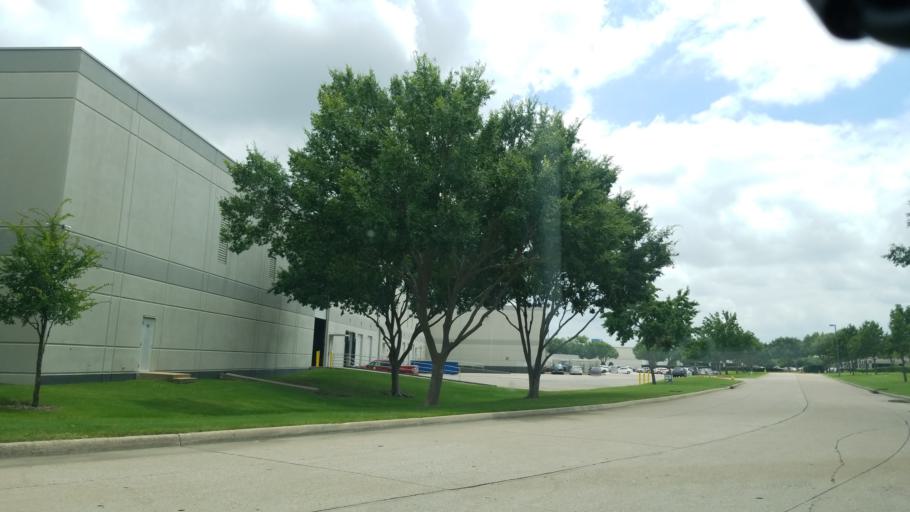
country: US
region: Texas
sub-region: Dallas County
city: Carrollton
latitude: 32.9502
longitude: -96.9360
